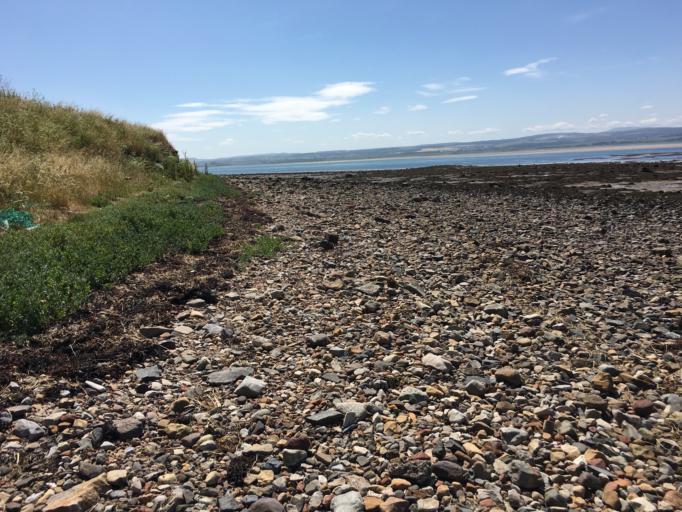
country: GB
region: England
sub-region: Northumberland
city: Belford
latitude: 55.6724
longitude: -1.8066
